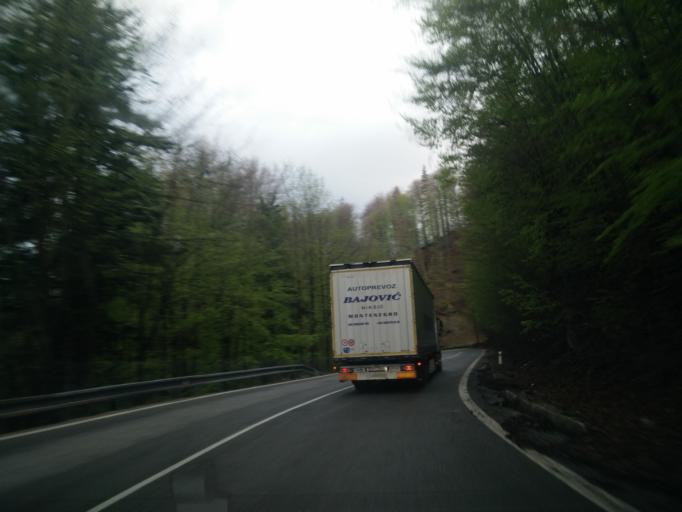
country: SK
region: Banskobystricky
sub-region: Okres Ziar nad Hronom
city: Kremnica
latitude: 48.8323
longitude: 19.0170
